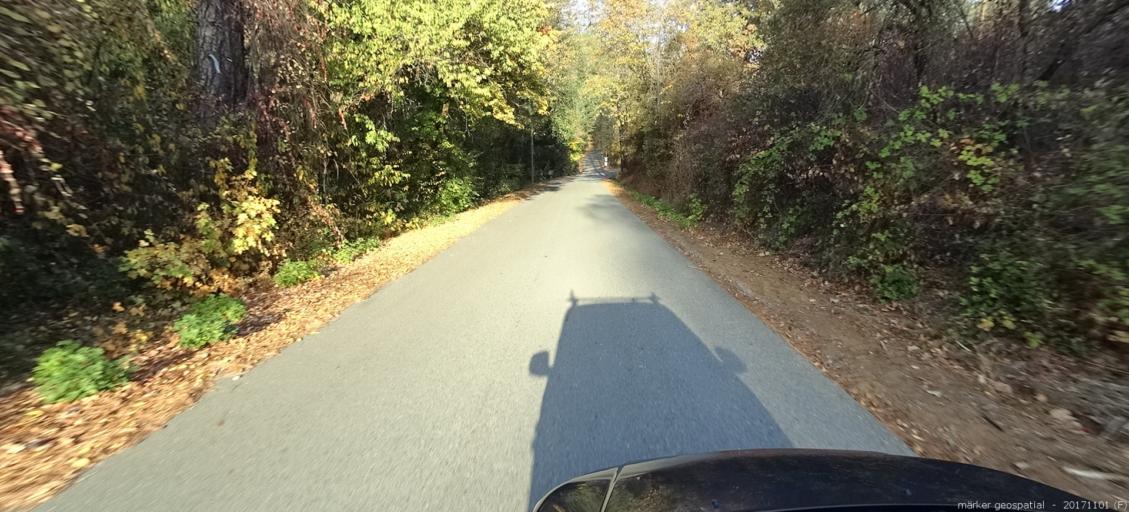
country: US
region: California
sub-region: Shasta County
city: Shasta Lake
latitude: 40.8143
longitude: -122.3275
